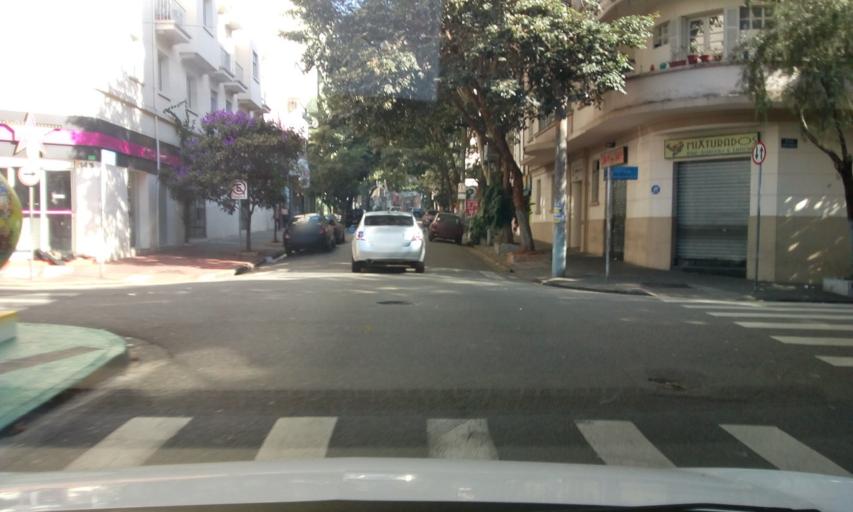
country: BR
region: Sao Paulo
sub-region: Sao Paulo
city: Sao Paulo
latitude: -23.5403
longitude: -46.6515
